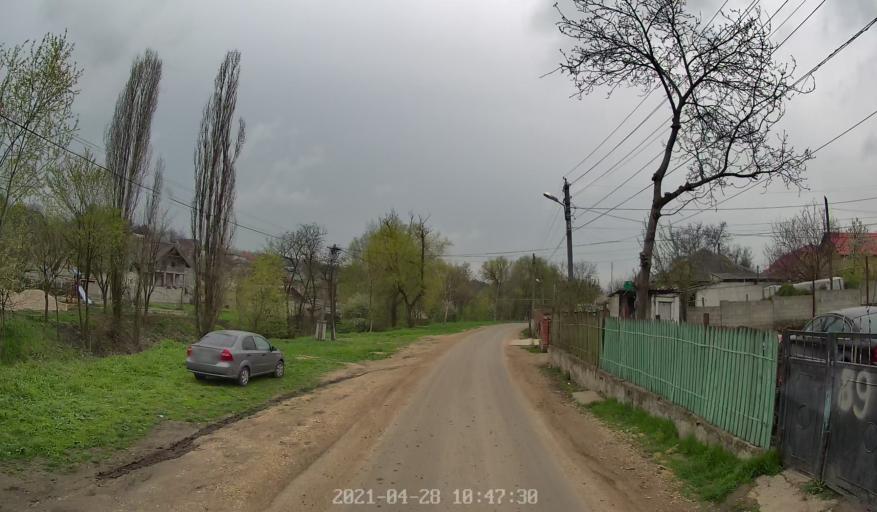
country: MD
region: Chisinau
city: Singera
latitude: 46.9887
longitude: 28.9479
